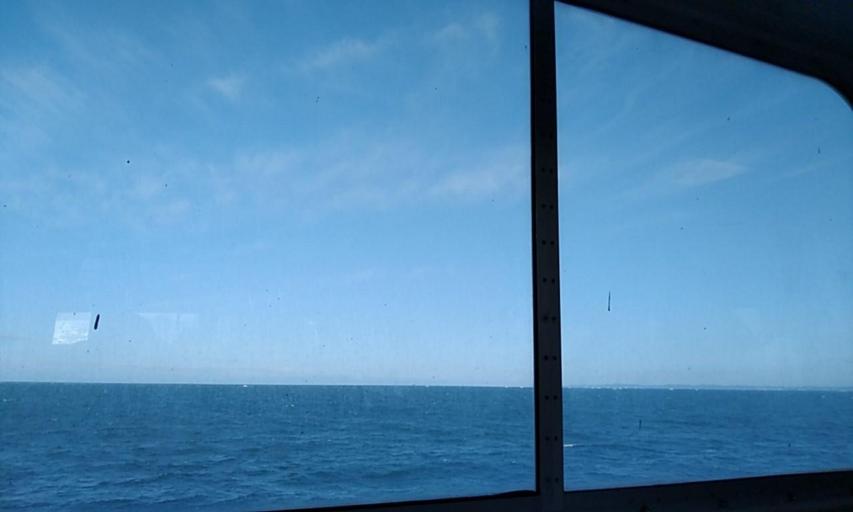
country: JP
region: Mie
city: Toba
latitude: 34.5476
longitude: 136.9632
